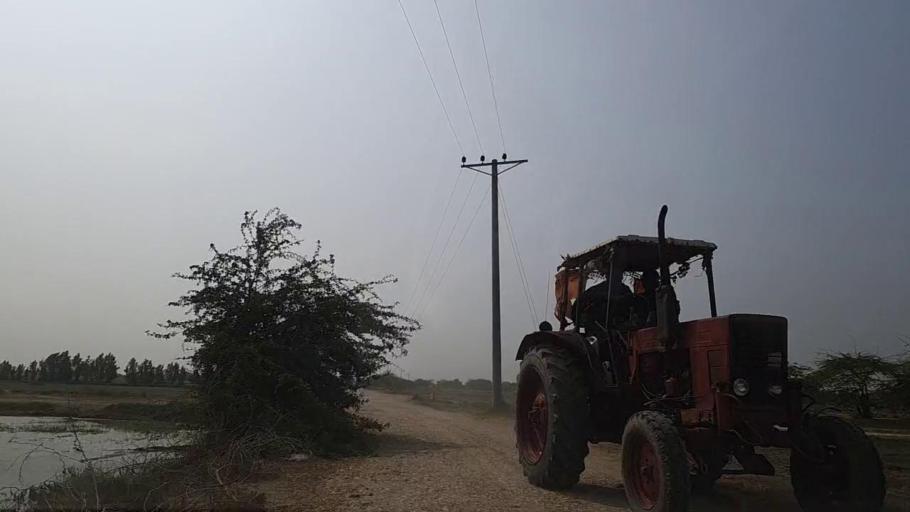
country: PK
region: Sindh
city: Mirpur Sakro
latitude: 24.6124
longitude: 67.7296
